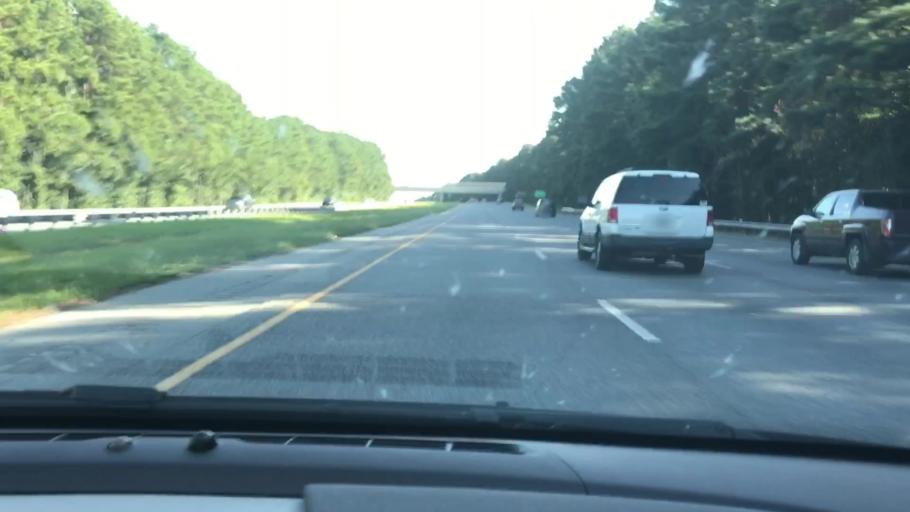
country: US
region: Alabama
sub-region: Russell County
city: Phenix City
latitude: 32.5602
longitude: -84.9626
